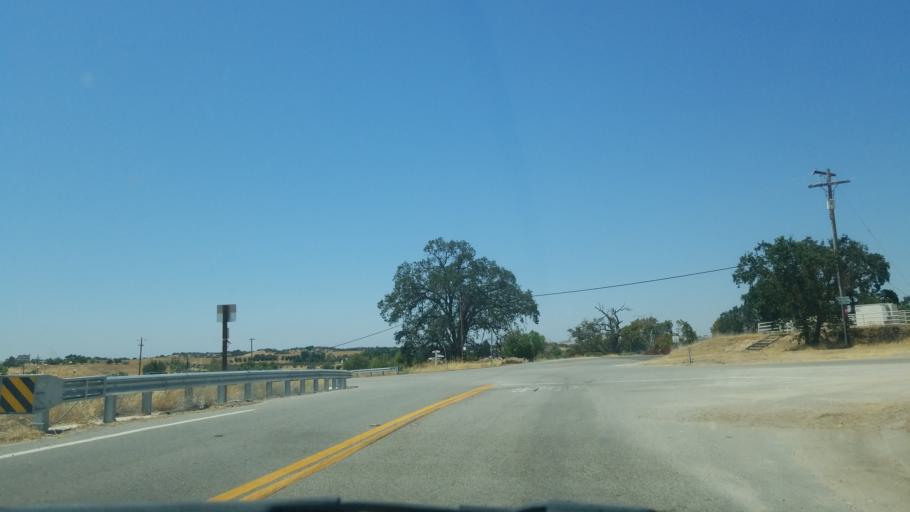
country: US
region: California
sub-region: San Luis Obispo County
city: Atascadero
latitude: 35.5341
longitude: -120.5234
